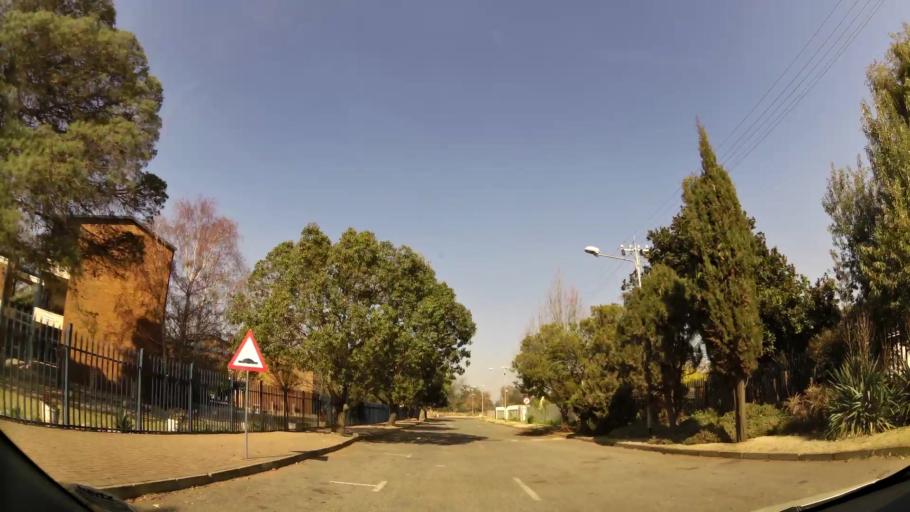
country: ZA
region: Gauteng
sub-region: West Rand District Municipality
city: Randfontein
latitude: -26.1587
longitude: 27.7041
